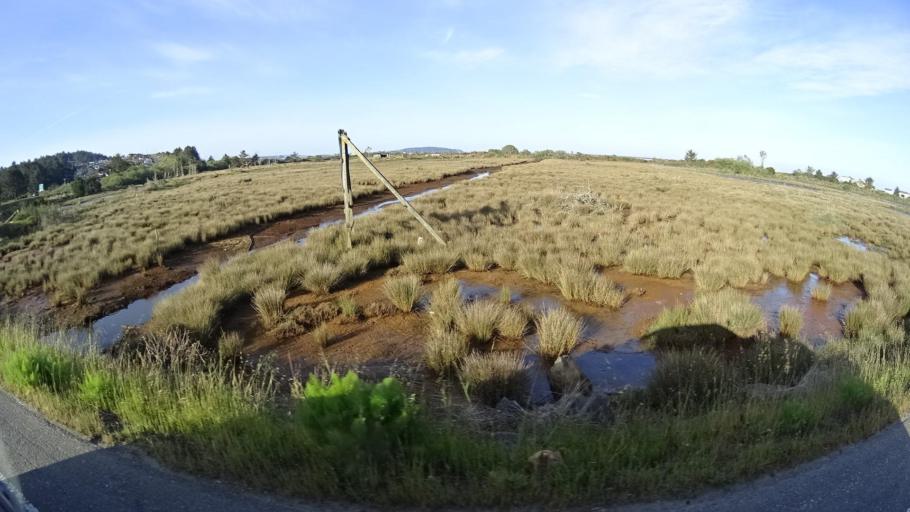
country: US
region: California
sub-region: Humboldt County
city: Humboldt Hill
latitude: 40.7376
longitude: -124.2117
